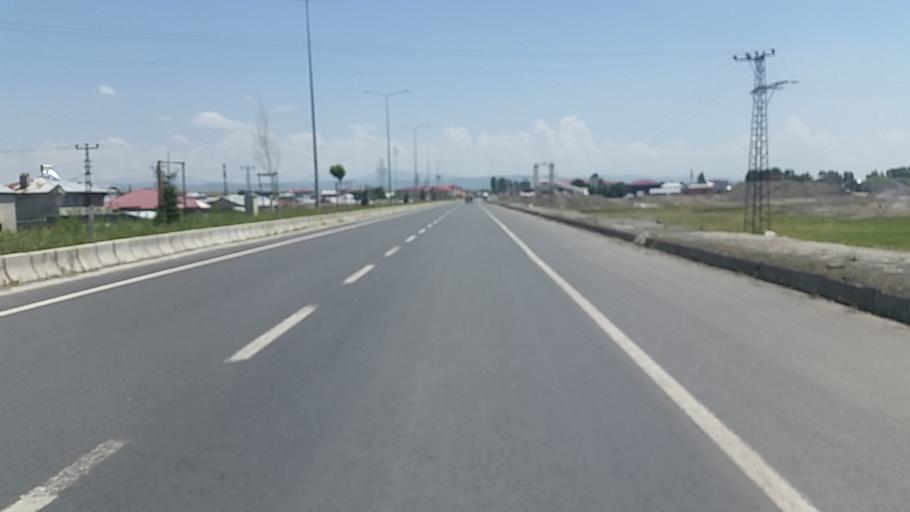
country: TR
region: Agri
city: Agri
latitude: 39.7109
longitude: 43.0737
